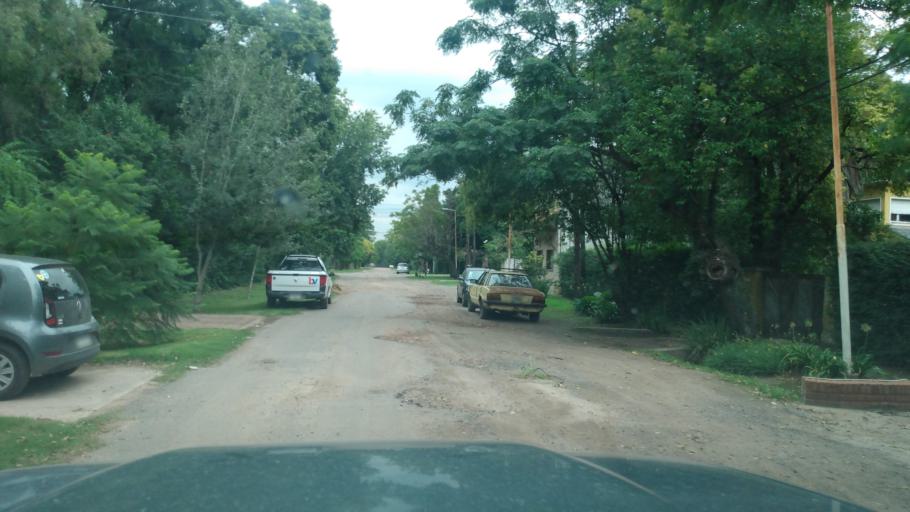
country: AR
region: Buenos Aires
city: Hurlingham
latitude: -34.5720
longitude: -58.6941
